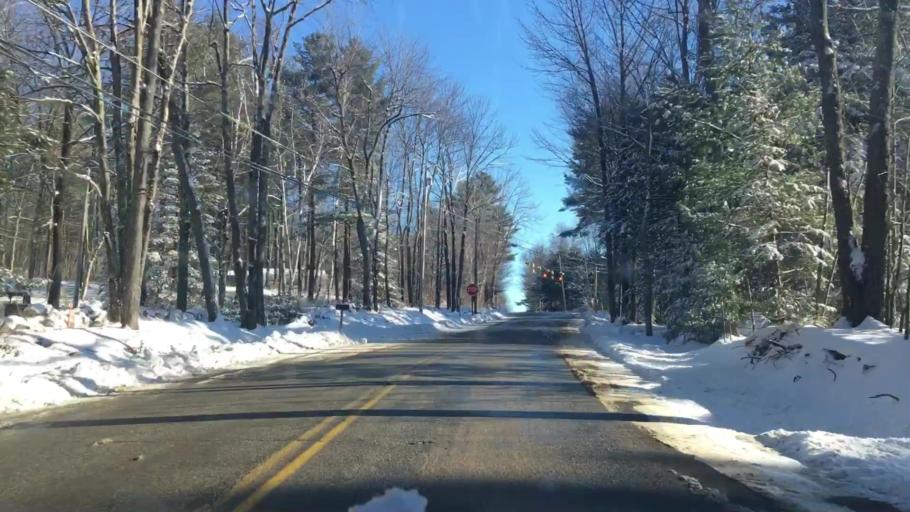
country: US
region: Maine
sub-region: Cumberland County
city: New Gloucester
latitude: 43.9493
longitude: -70.3038
